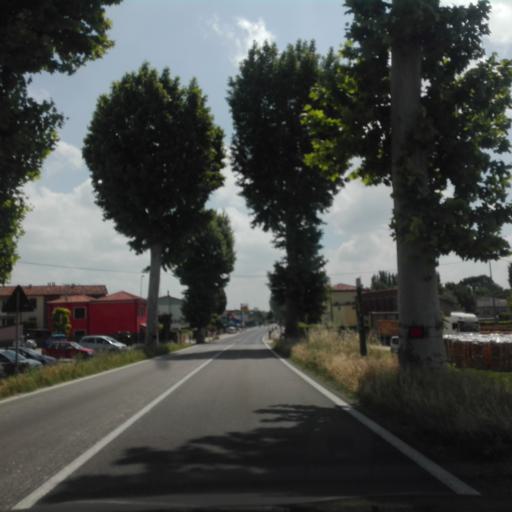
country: IT
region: Veneto
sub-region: Provincia di Rovigo
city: Villadose
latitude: 45.0706
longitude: 11.8847
